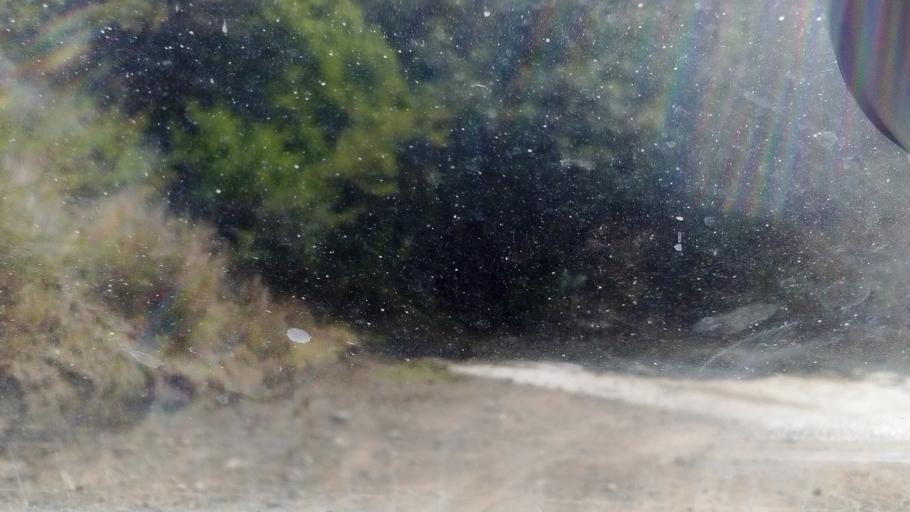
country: MX
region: Guanajuato
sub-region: Silao de la Victoria
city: San Francisco (Banos de Agua Caliente)
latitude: 21.1729
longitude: -101.4583
